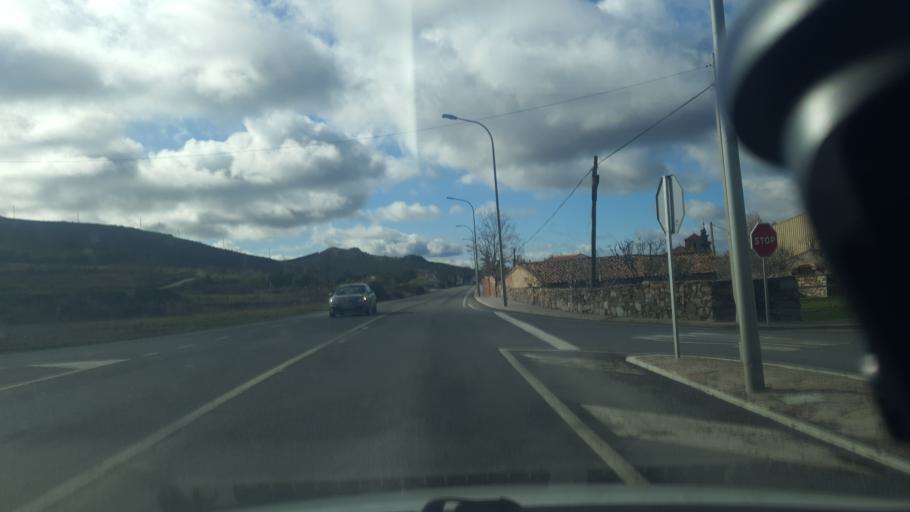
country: ES
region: Castille and Leon
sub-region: Provincia de Avila
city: Ojos-Albos
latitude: 40.7424
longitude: -4.4691
